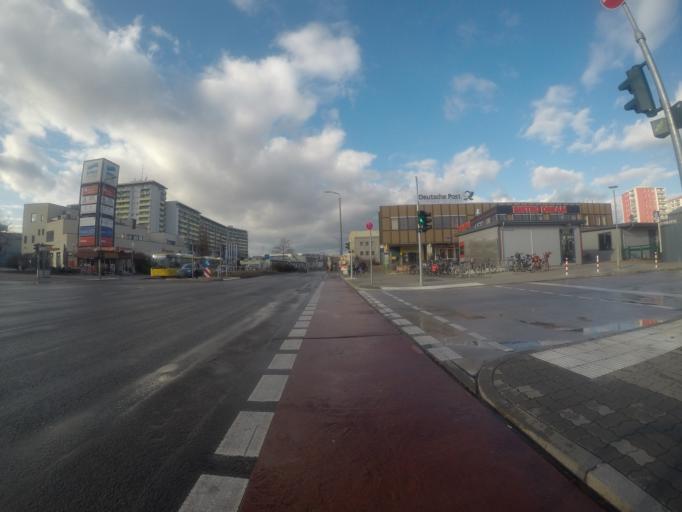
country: DE
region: Berlin
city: Kaulsdorf
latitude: 52.5207
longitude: 13.5882
